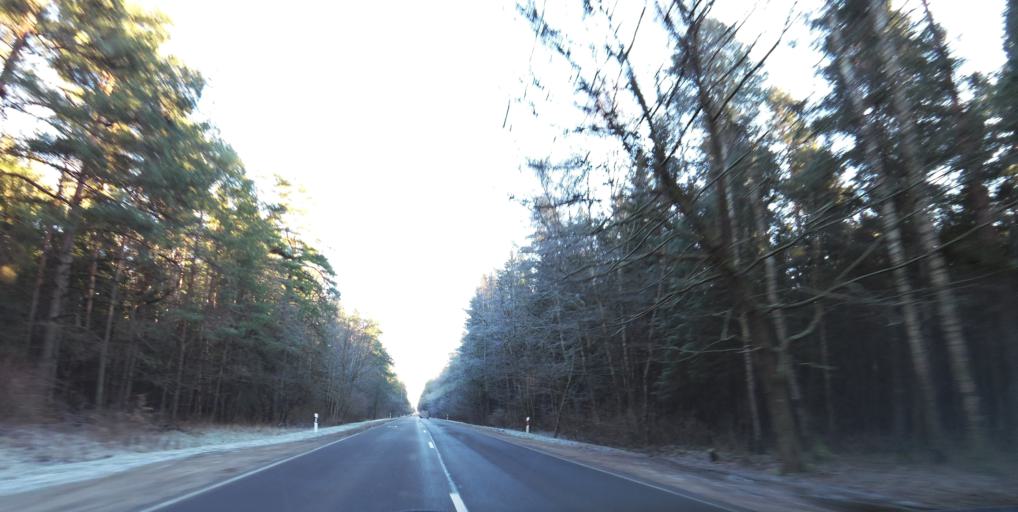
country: LT
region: Vilnius County
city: Lazdynai
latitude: 54.6439
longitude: 25.1576
